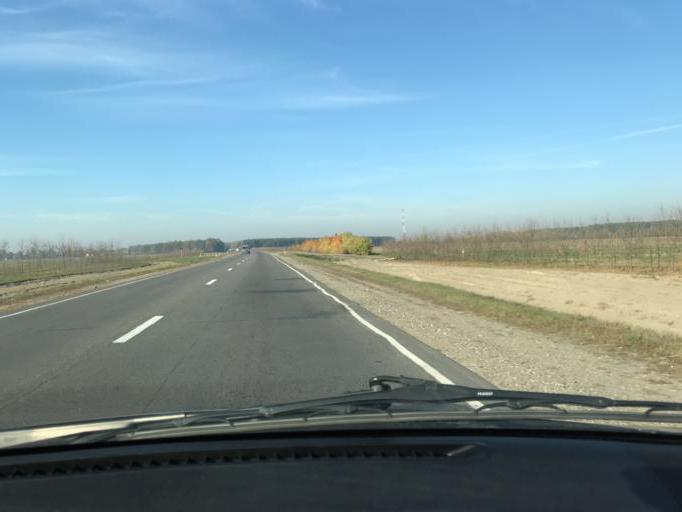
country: BY
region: Brest
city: Luninyets
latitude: 52.2747
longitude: 26.9772
